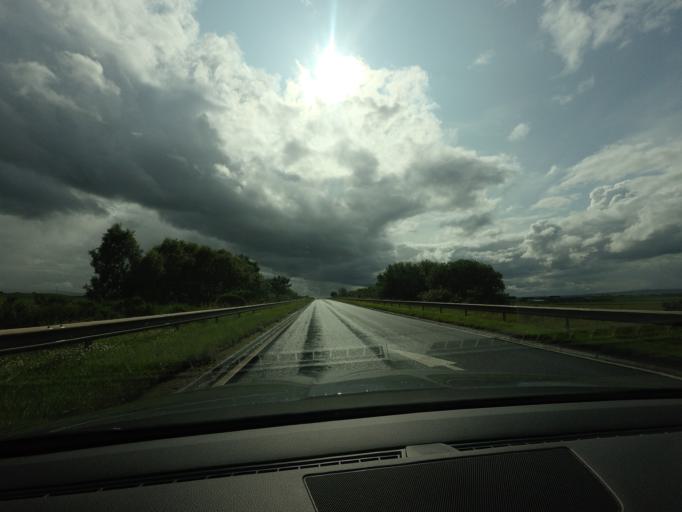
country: GB
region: Scotland
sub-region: Highland
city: Nairn
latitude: 57.5570
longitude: -3.9704
